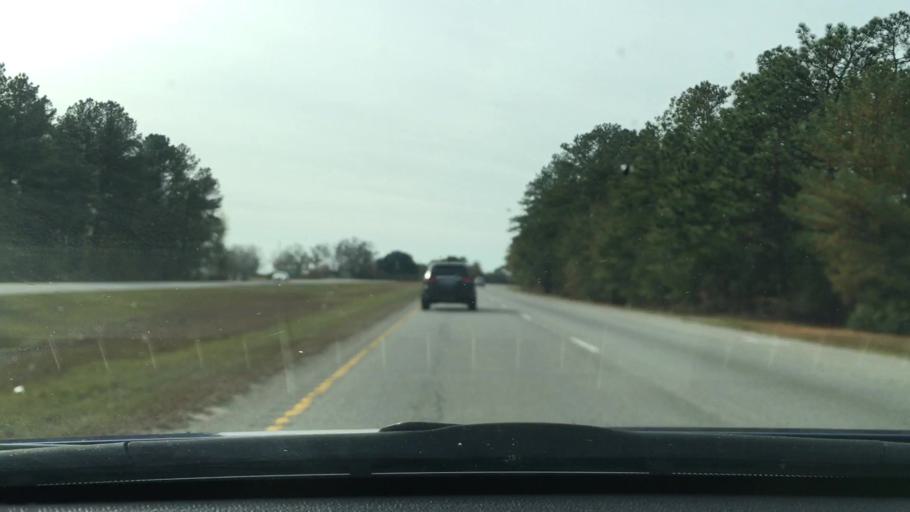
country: US
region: South Carolina
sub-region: Richland County
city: Gadsden
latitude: 33.9409
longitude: -80.7002
